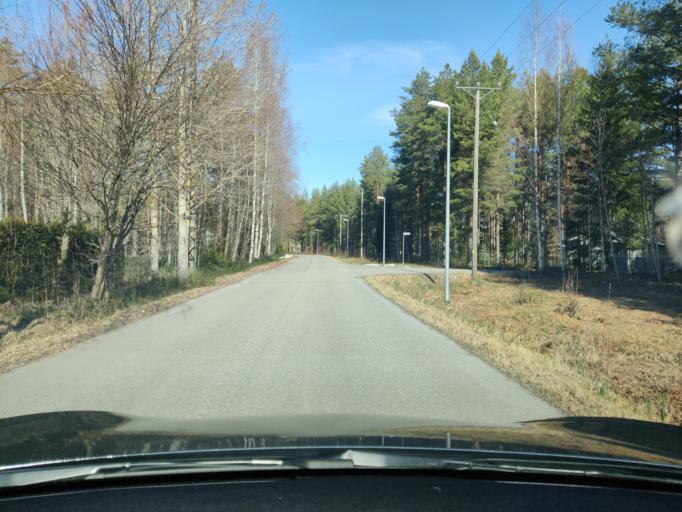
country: FI
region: Northern Savo
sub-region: Kuopio
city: Vehmersalmi
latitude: 62.7708
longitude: 27.9860
